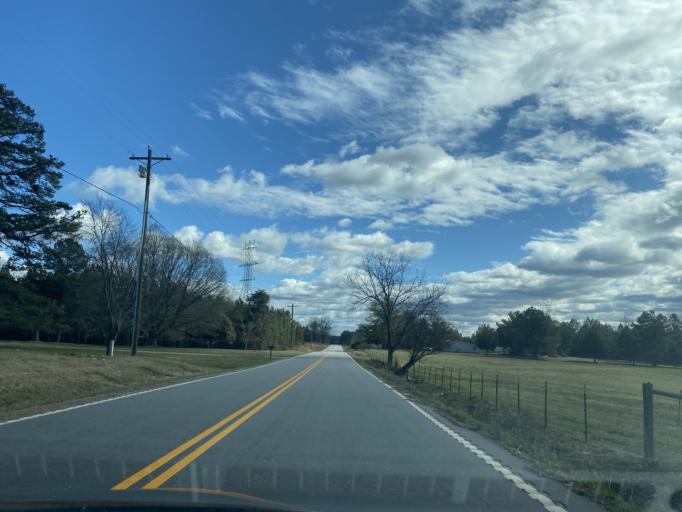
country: US
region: South Carolina
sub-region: Spartanburg County
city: Cowpens
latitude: 35.0985
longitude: -81.7566
